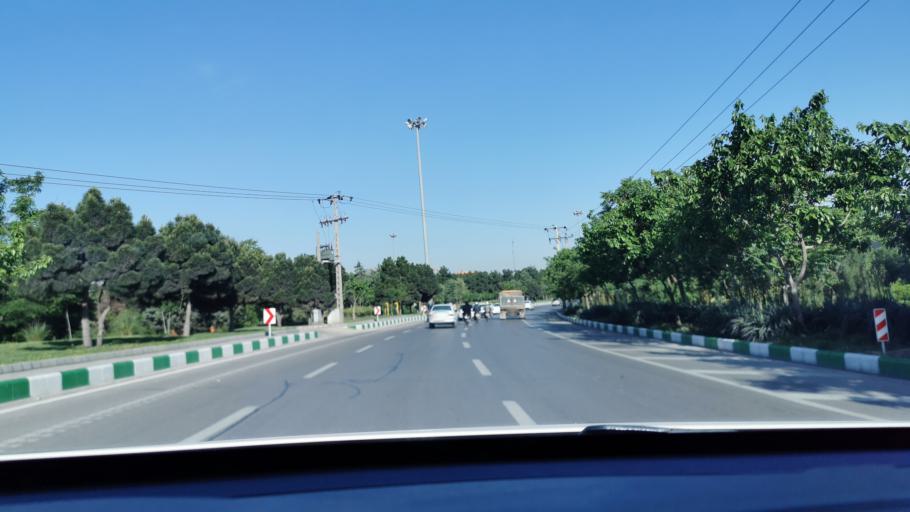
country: IR
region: Razavi Khorasan
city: Mashhad
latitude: 36.2509
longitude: 59.6102
